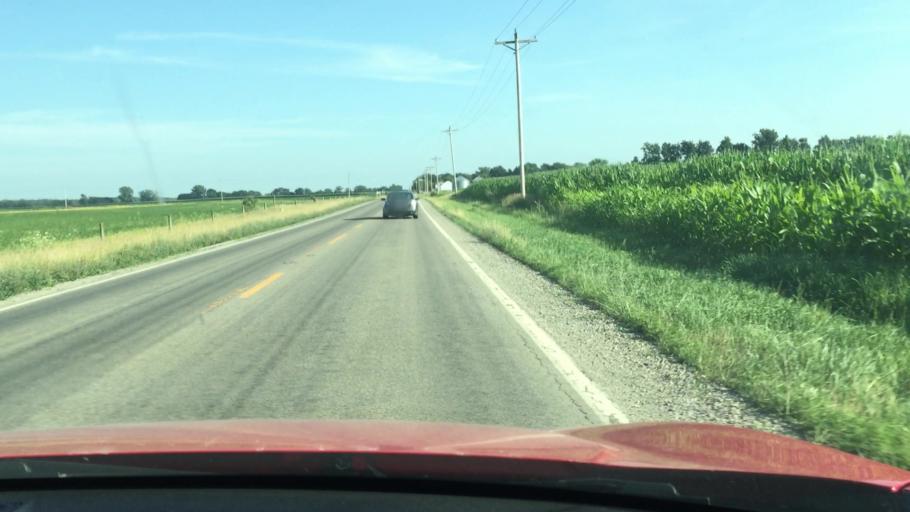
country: US
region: Ohio
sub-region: Hardin County
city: Ada
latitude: 40.6632
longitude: -83.8523
